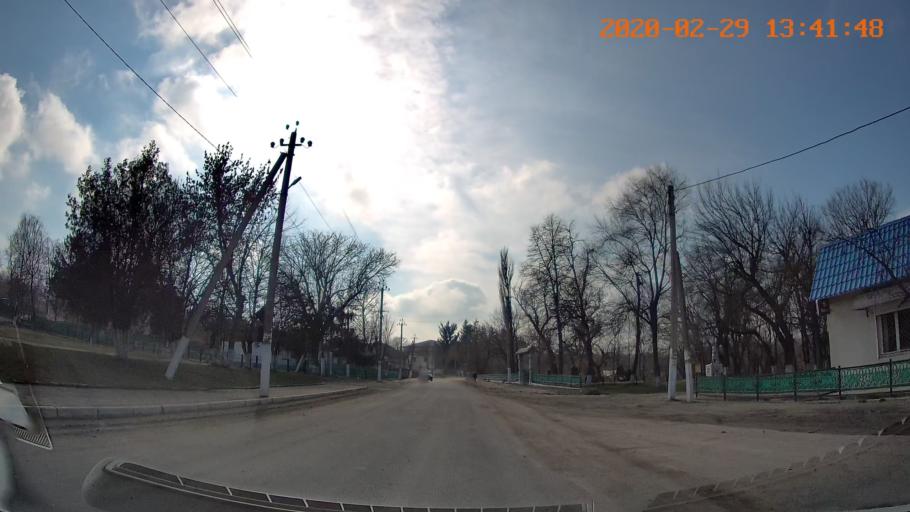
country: MD
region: Floresti
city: Leninskiy
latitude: 47.8438
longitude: 28.5552
